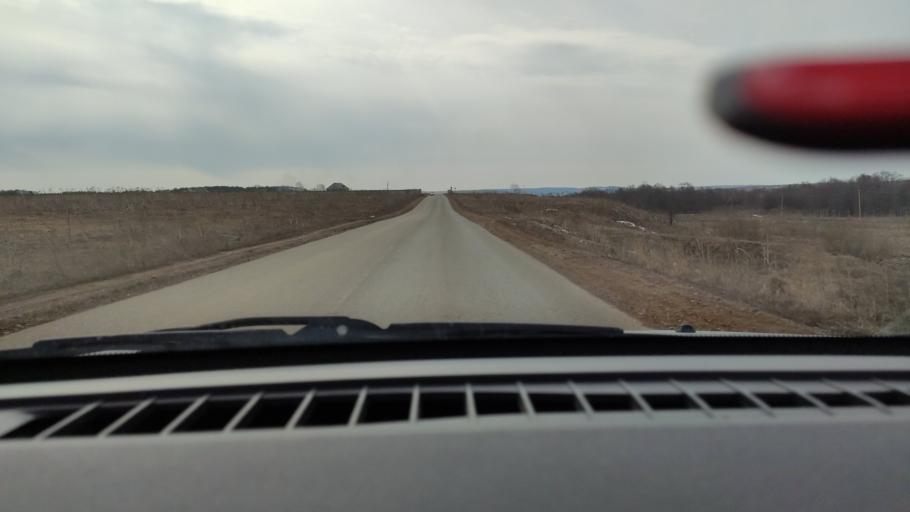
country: RU
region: Perm
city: Kultayevo
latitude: 57.9028
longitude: 55.9924
